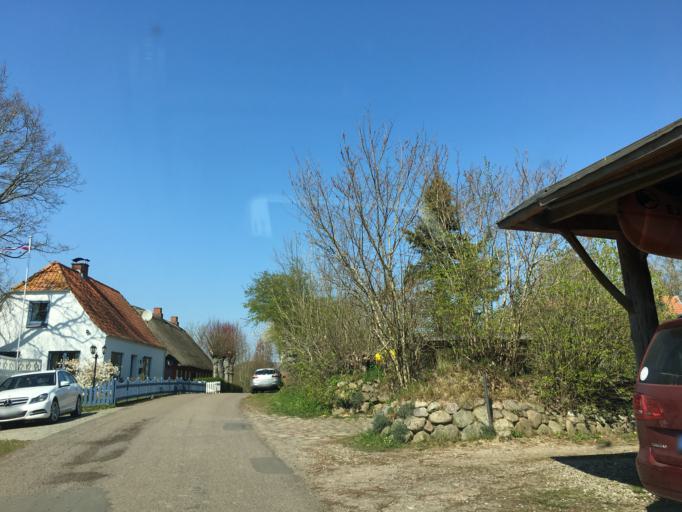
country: DE
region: Schleswig-Holstein
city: Nottfeld
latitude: 54.5950
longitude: 9.7994
